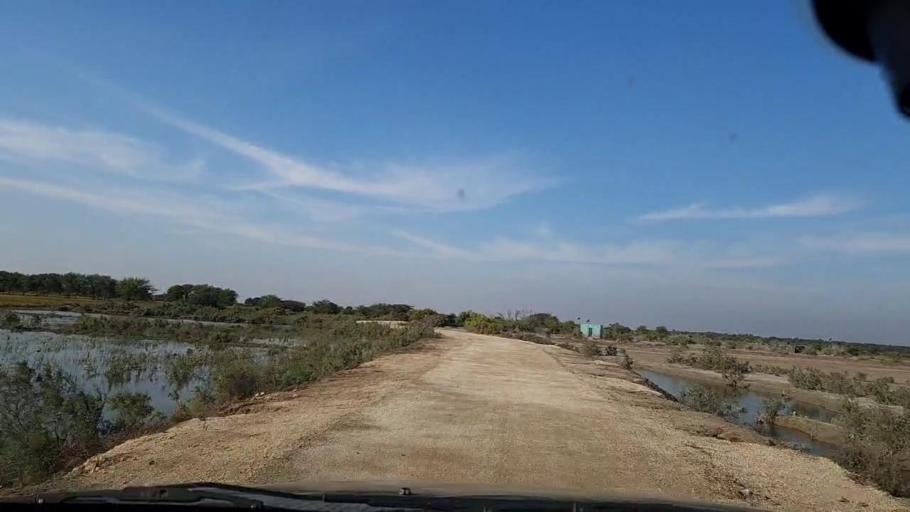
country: PK
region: Sindh
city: Mirpur Batoro
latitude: 24.6357
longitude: 68.2982
